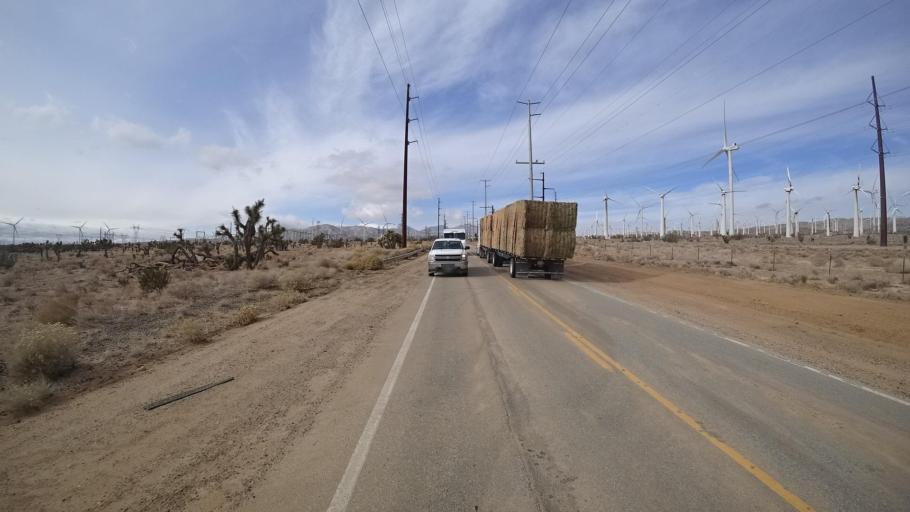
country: US
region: California
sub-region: Kern County
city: Mojave
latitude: 35.0384
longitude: -118.2719
